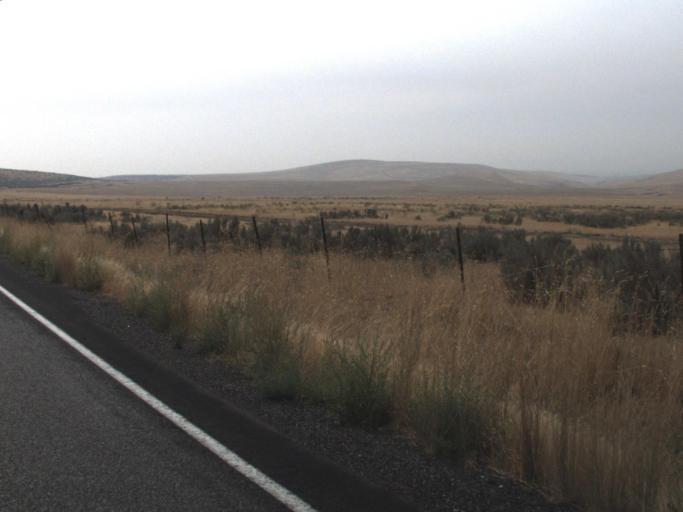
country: US
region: Washington
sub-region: Yakima County
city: Sunnyside
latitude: 46.4396
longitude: -119.9372
